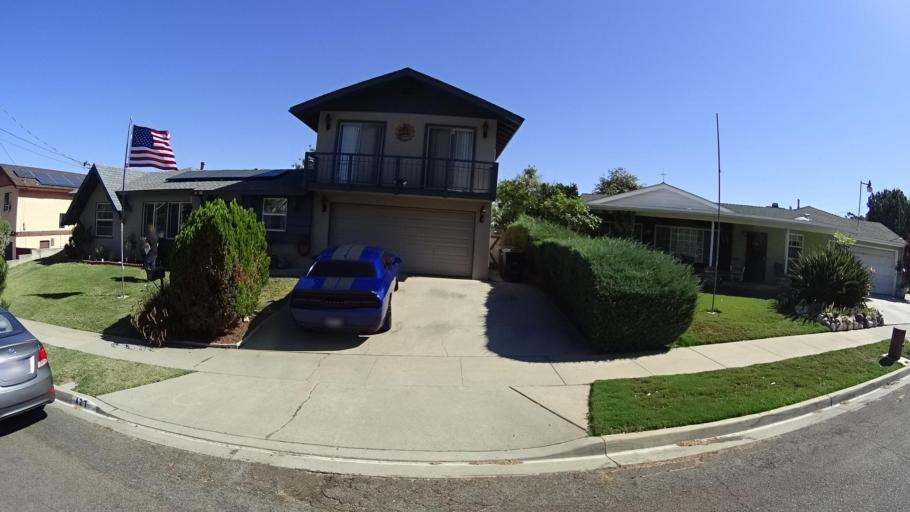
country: US
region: California
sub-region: San Diego County
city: La Presa
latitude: 32.7012
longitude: -117.0186
